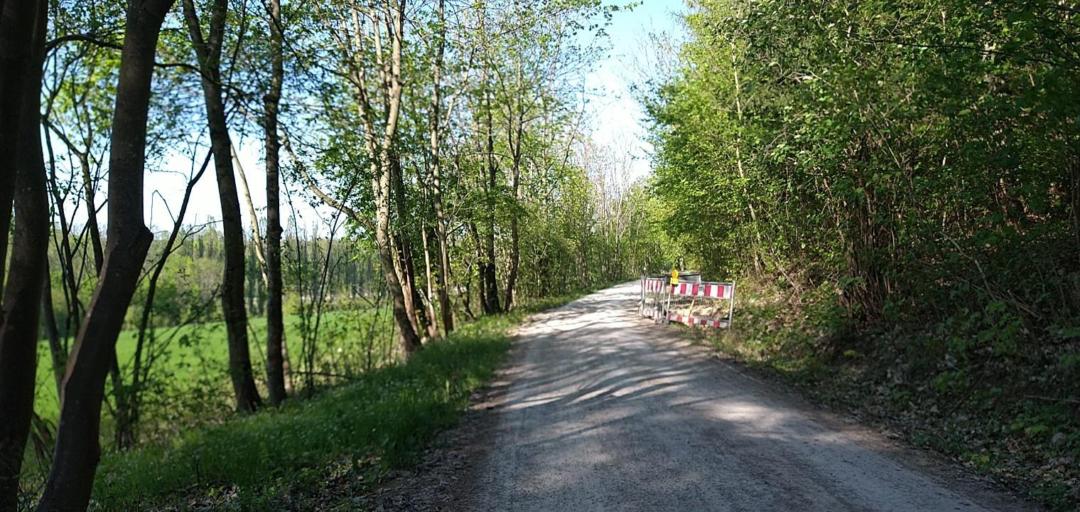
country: DE
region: Thuringia
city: Kiliansroda
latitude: 50.9226
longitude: 11.3793
